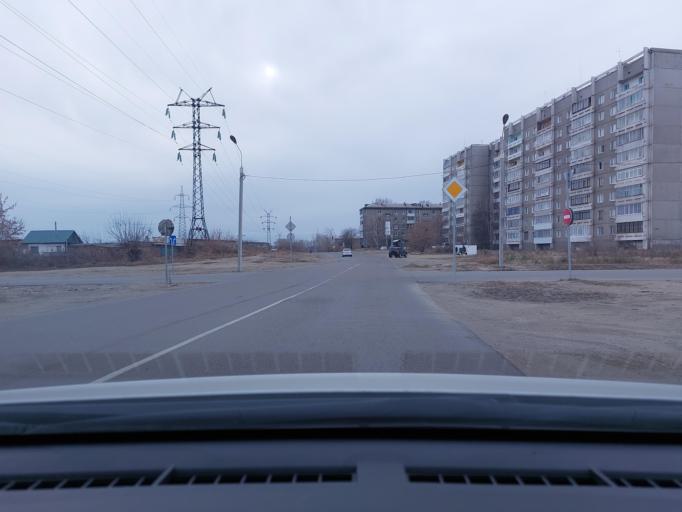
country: RU
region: Irkutsk
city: Smolenshchina
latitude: 52.3472
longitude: 104.1663
